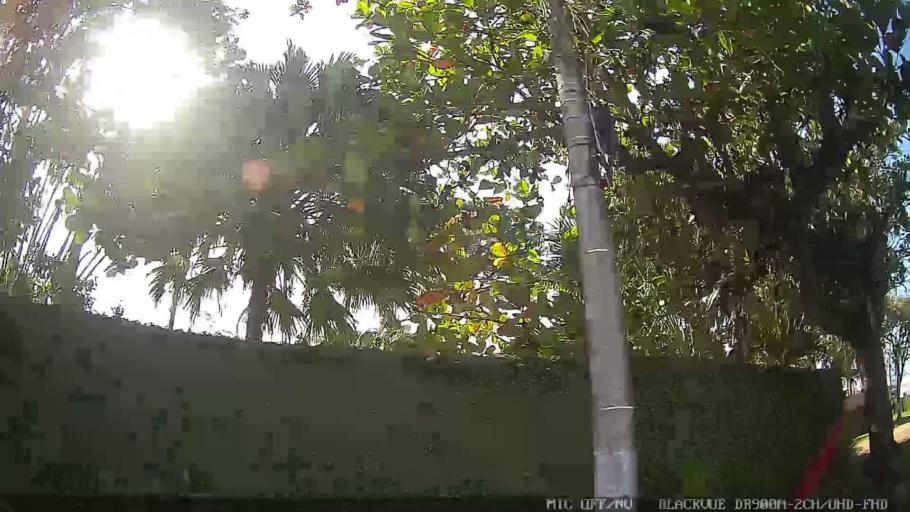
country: BR
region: Sao Paulo
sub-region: Guaruja
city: Guaruja
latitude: -23.9809
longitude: -46.2107
